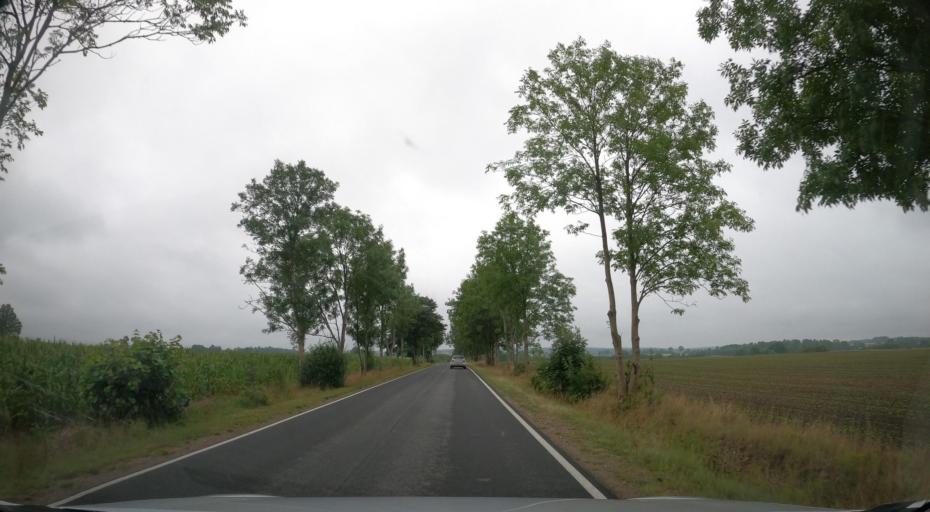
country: PL
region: Pomeranian Voivodeship
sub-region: Powiat wejherowski
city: Linia
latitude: 54.4740
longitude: 17.8552
